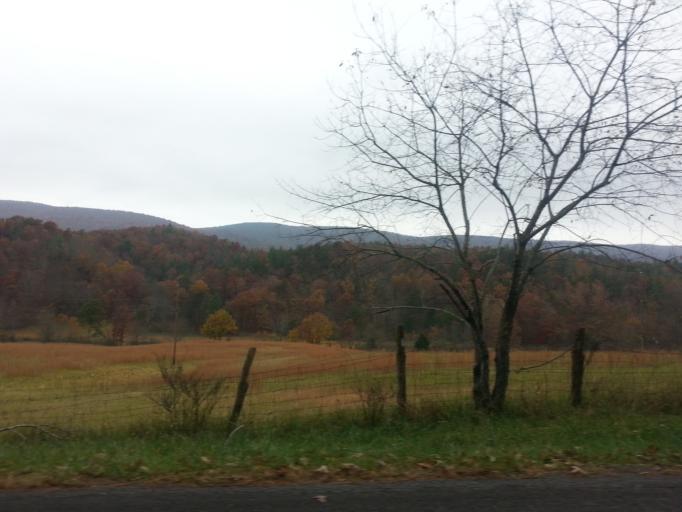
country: US
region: Virginia
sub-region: Bland County
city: Bland
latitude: 37.0441
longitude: -81.0700
